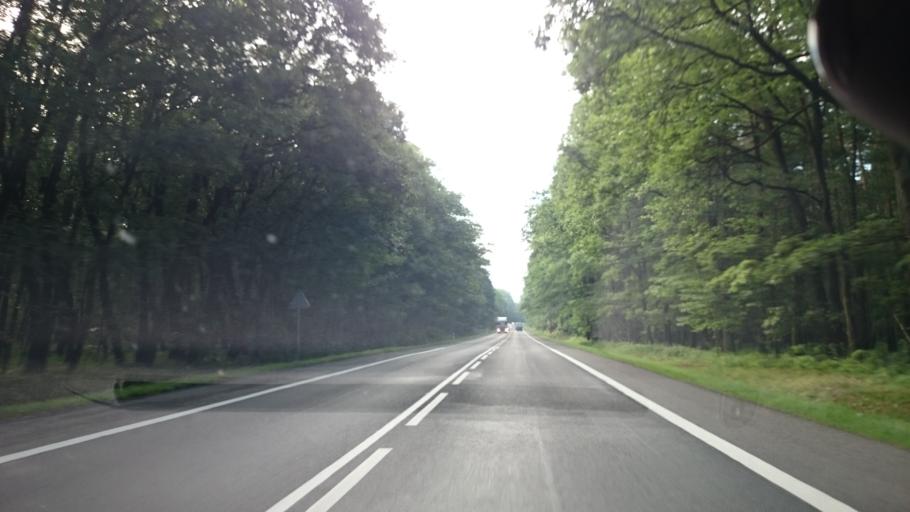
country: PL
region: Opole Voivodeship
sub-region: Powiat opolski
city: Chrzastowice
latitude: 50.6206
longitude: 18.0570
